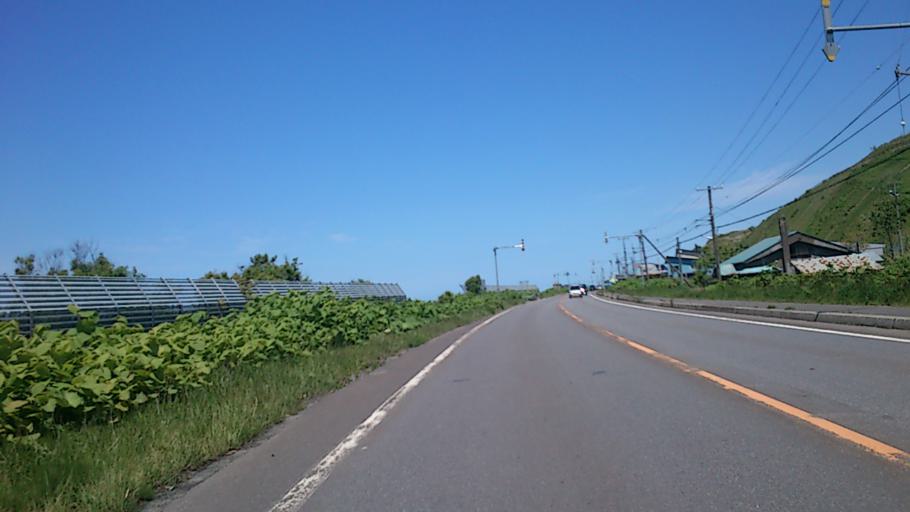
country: JP
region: Hokkaido
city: Rumoi
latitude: 43.9725
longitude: 141.6467
